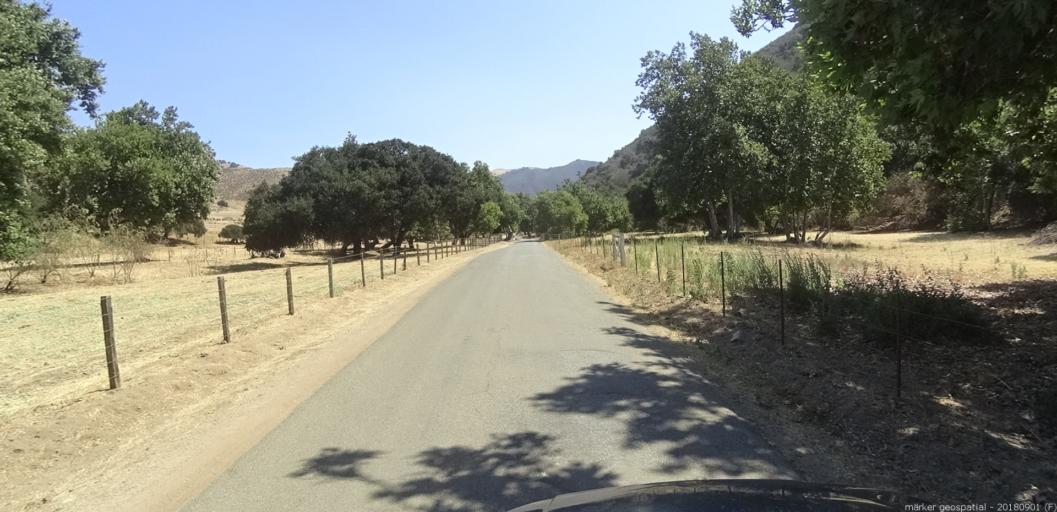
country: US
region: California
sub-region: Monterey County
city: Gonzales
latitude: 36.6032
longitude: -121.4199
